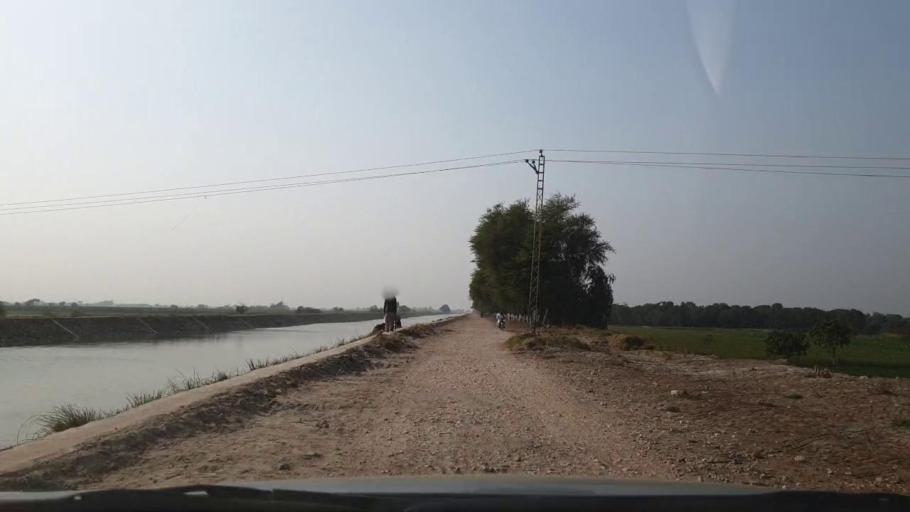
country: PK
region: Sindh
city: Tando Adam
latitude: 25.6393
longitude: 68.5896
